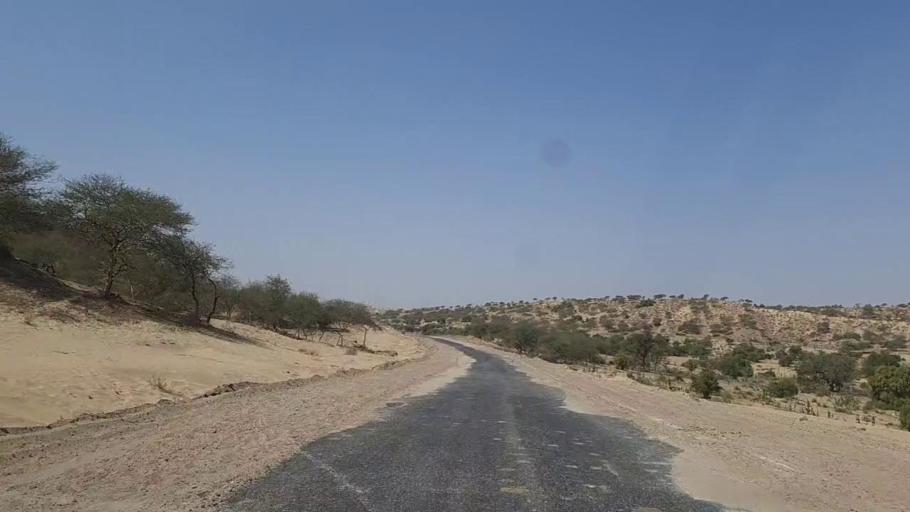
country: PK
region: Sindh
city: Diplo
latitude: 24.5883
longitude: 69.5466
